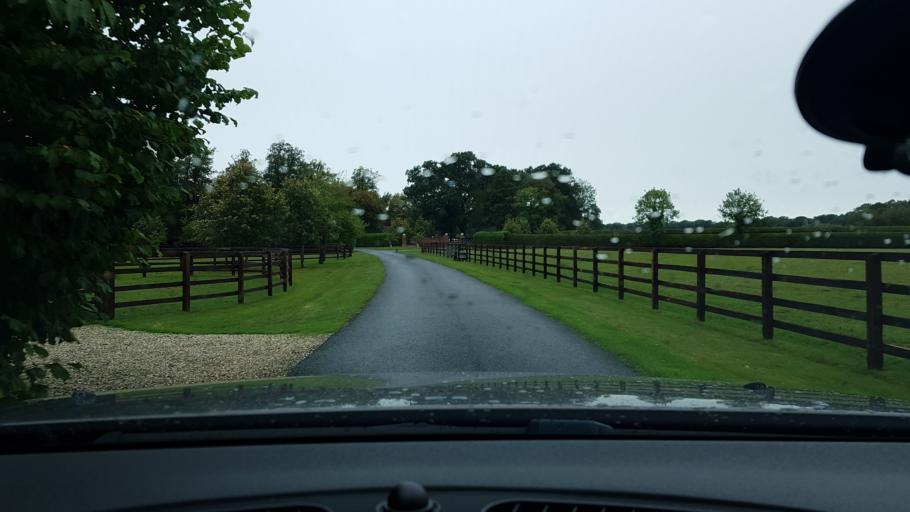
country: GB
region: England
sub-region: West Berkshire
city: Hungerford
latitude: 51.4233
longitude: -1.4818
